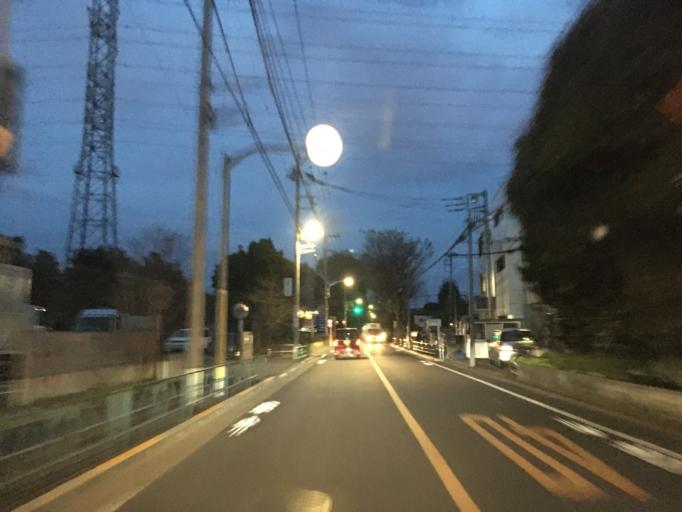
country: JP
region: Tokyo
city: Mitaka-shi
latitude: 35.6832
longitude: 139.5405
